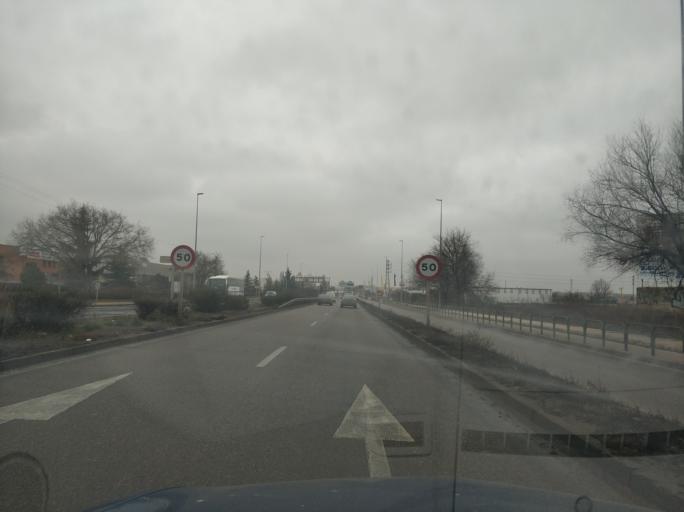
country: ES
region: Castille and Leon
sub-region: Provincia de Valladolid
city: Cisterniga
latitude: 41.6273
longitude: -4.7001
